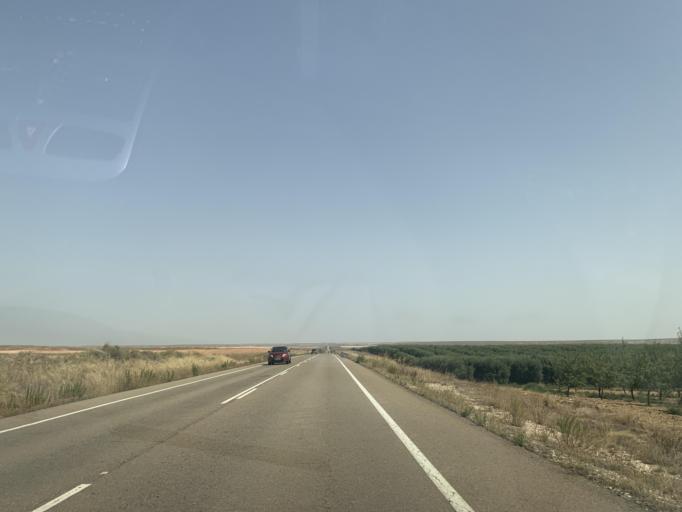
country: ES
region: Aragon
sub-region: Provincia de Zaragoza
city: Belchite
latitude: 41.3564
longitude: -0.7359
